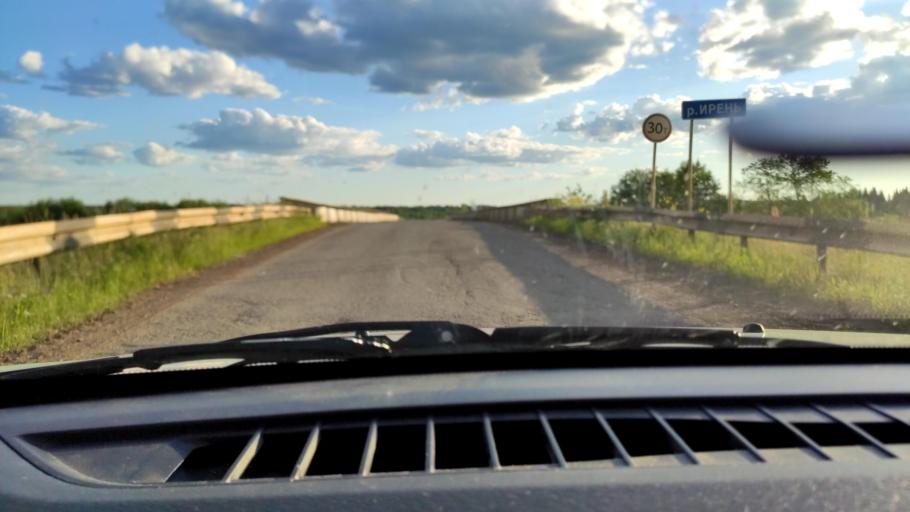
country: RU
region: Perm
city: Uinskoye
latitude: 57.0755
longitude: 56.5986
